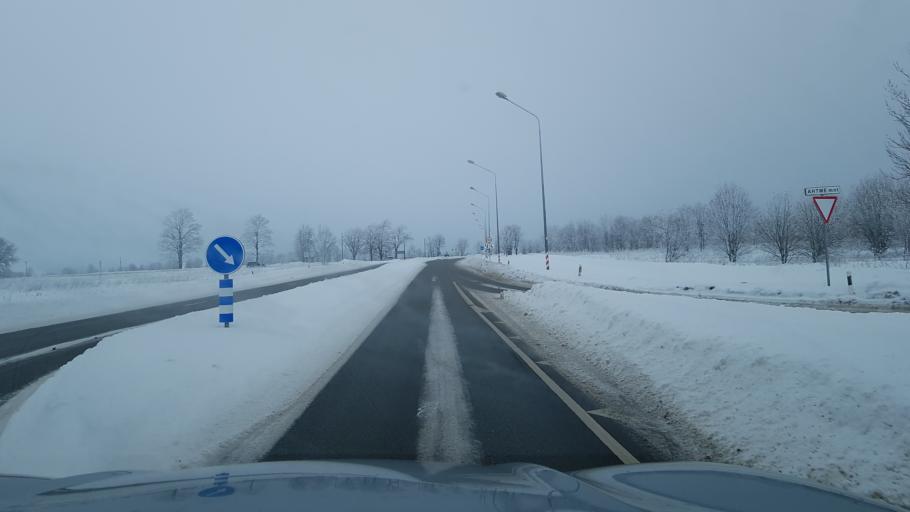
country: EE
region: Ida-Virumaa
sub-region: Johvi vald
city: Johvi
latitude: 59.3363
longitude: 27.4030
